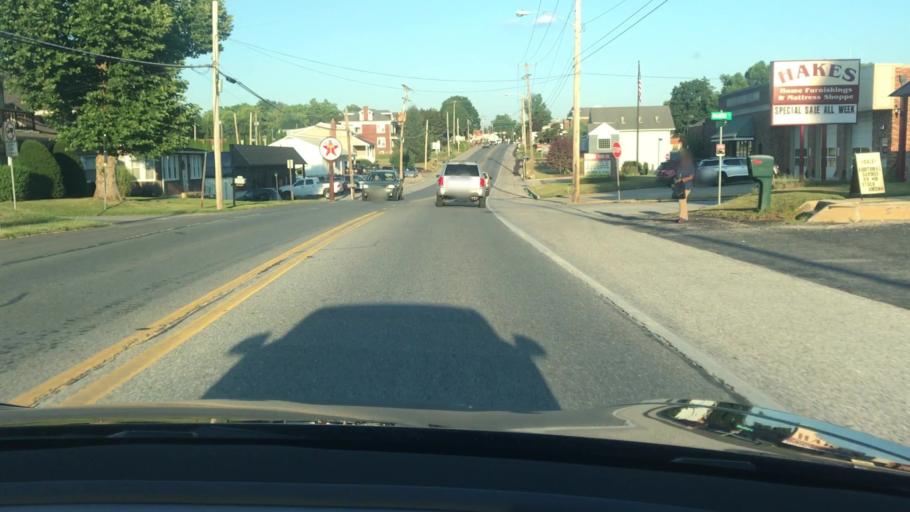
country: US
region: Pennsylvania
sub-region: York County
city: Shiloh
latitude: 39.9781
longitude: -76.7973
